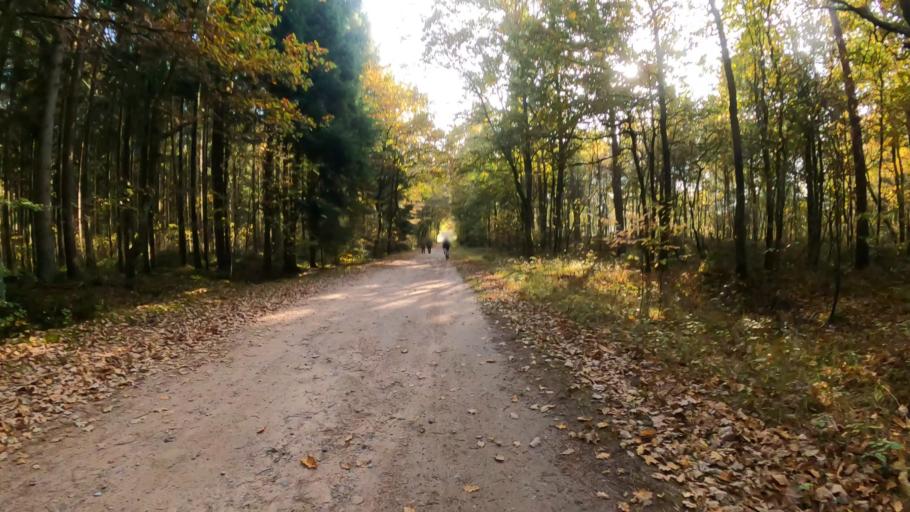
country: DE
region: Lower Saxony
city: Neu Wulmstorf
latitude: 53.4142
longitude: 9.8126
